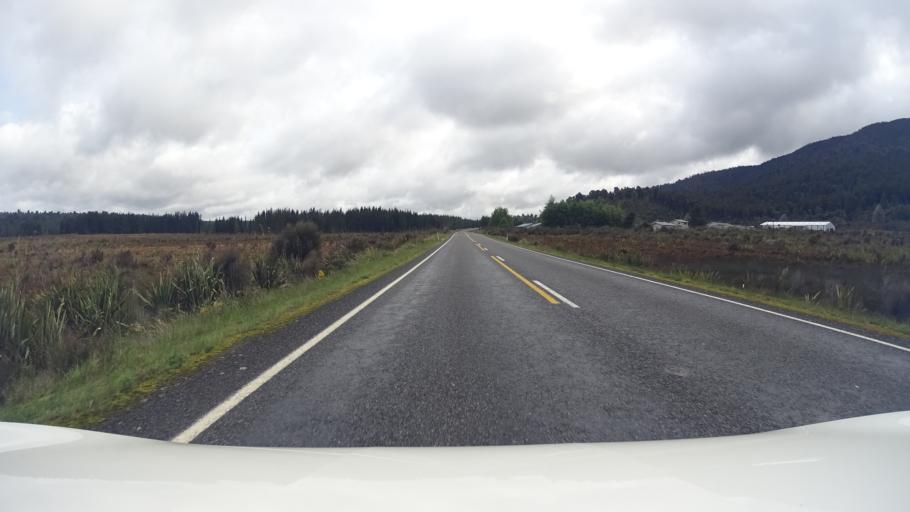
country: NZ
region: Manawatu-Wanganui
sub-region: Ruapehu District
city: Waiouru
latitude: -39.2290
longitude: 175.3951
